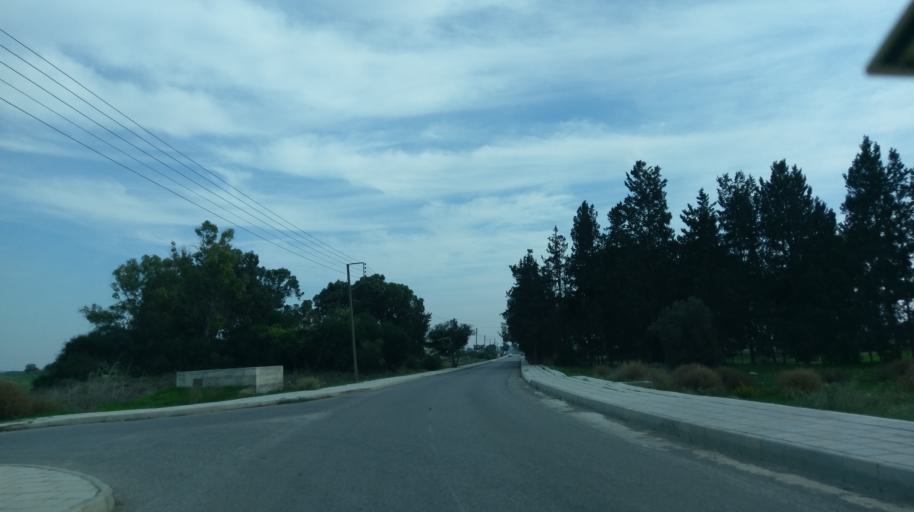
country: CY
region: Lefkosia
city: Mammari
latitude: 35.2304
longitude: 33.1688
